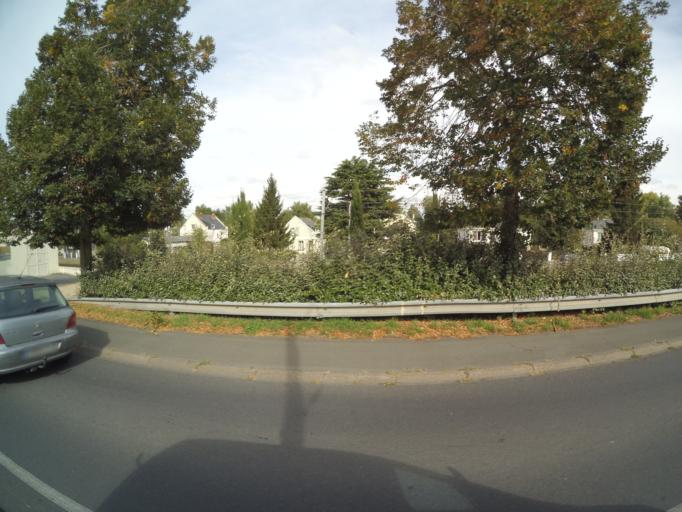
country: FR
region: Pays de la Loire
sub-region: Departement de Maine-et-Loire
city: Saumur
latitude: 47.2652
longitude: -0.0648
